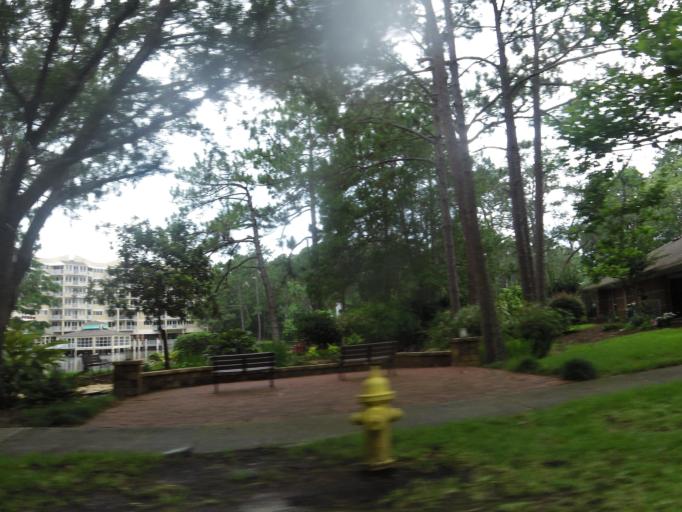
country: US
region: Florida
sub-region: Saint Johns County
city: Ponte Vedra Beach
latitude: 30.2549
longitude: -81.4548
